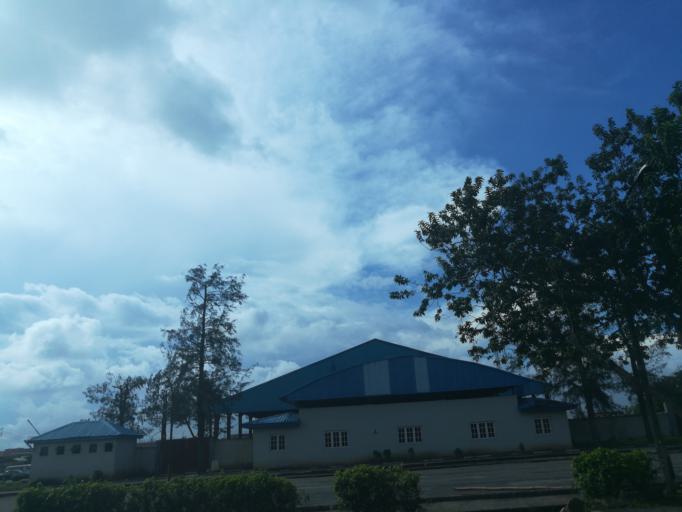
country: NG
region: Lagos
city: Ikeja
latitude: 6.6147
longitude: 3.3555
